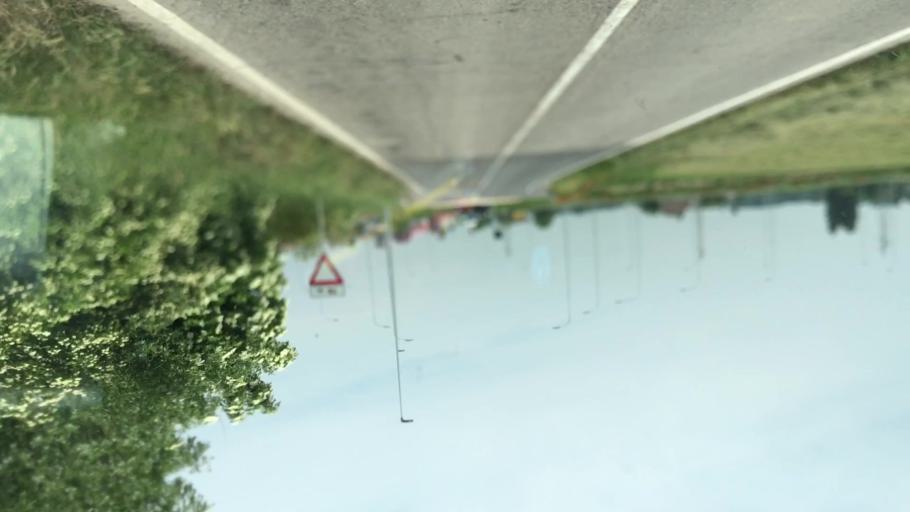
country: IT
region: Lombardy
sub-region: Provincia di Mantova
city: Campitello
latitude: 45.0819
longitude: 10.6004
